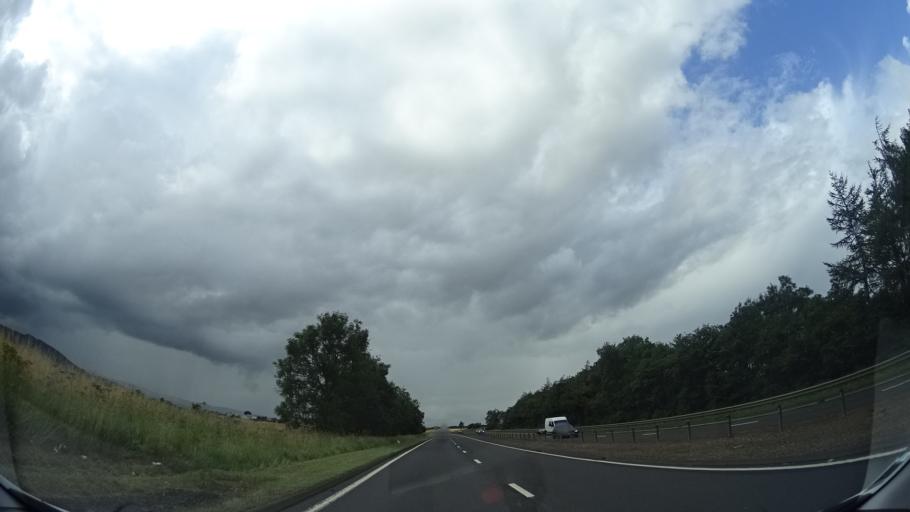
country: GB
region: Scotland
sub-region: Perth and Kinross
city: Auchterarder
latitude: 56.3338
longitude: -3.6249
